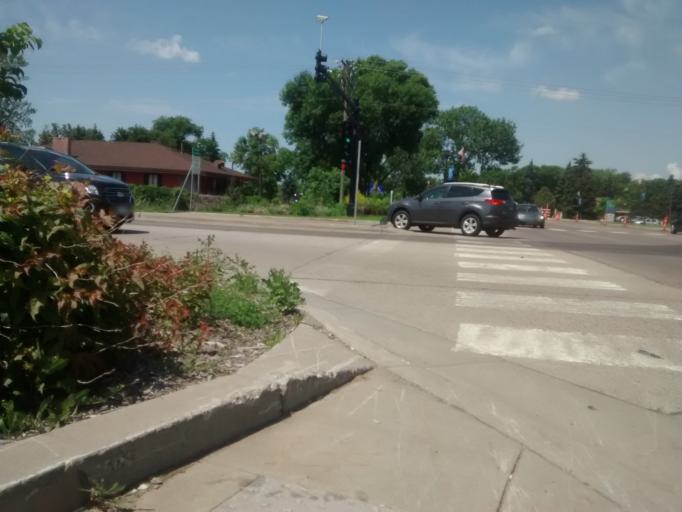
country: US
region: Minnesota
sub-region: Dakota County
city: Burnsville
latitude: 44.7698
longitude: -93.2899
